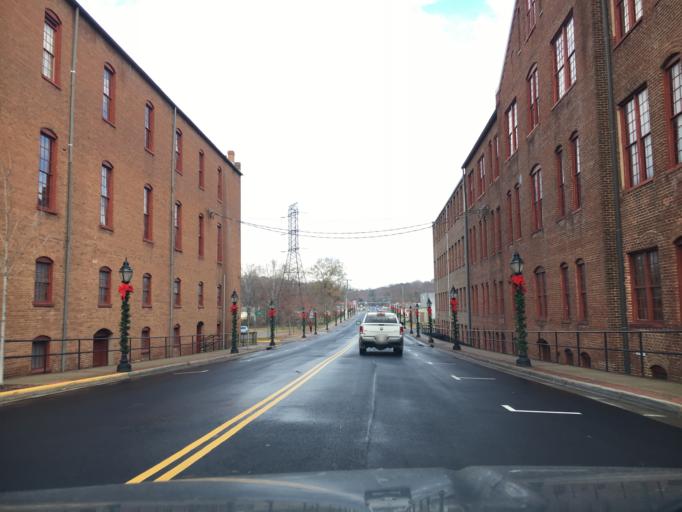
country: US
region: Virginia
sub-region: Prince Edward County
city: Farmville
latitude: 37.3049
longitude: -78.3907
